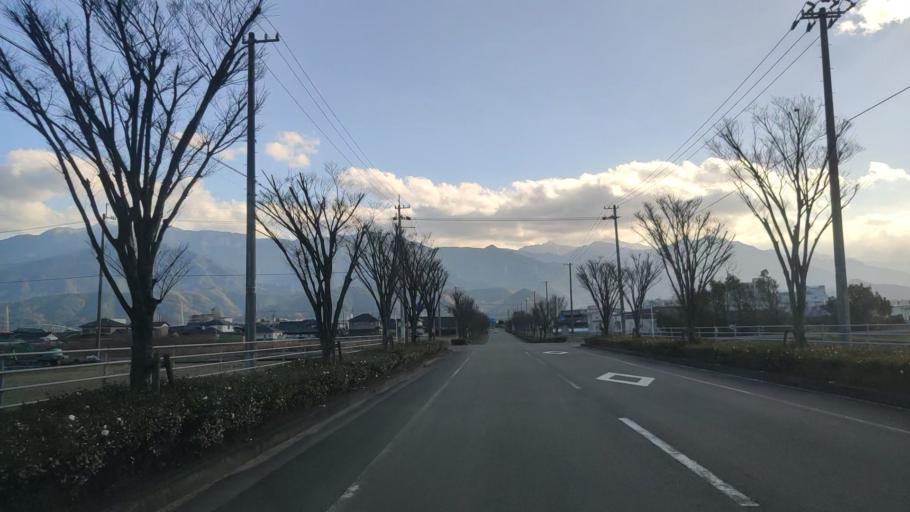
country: JP
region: Ehime
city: Saijo
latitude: 33.9343
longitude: 133.1927
